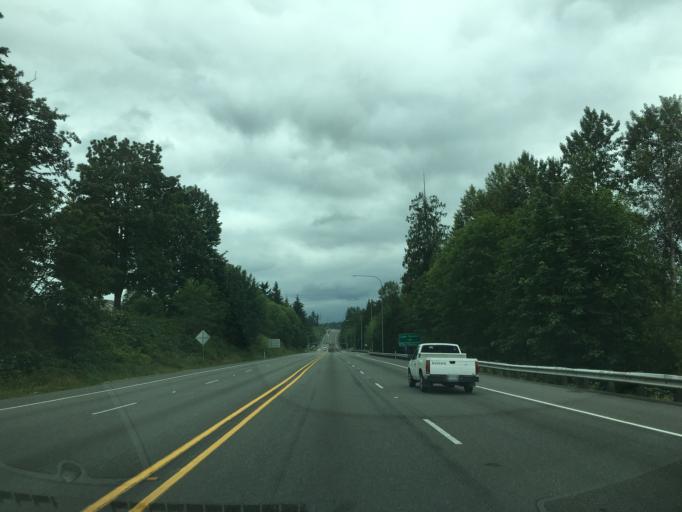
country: US
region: Washington
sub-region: Snohomish County
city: West Lake Stevens
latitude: 48.0089
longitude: -122.1073
